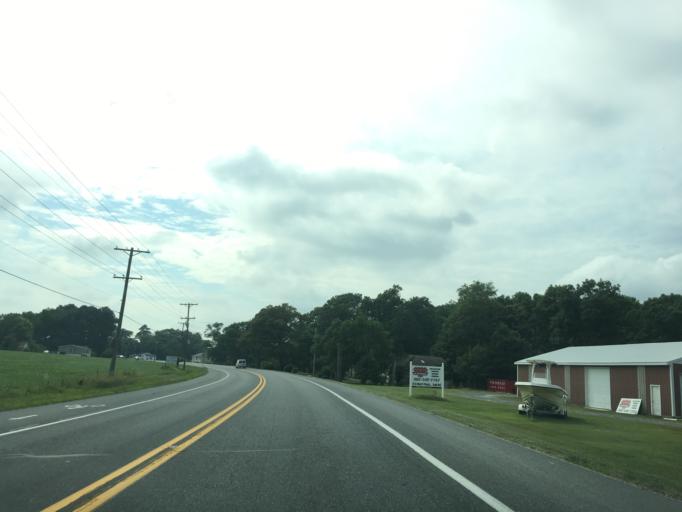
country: US
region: Delaware
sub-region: Sussex County
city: Long Neck
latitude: 38.5569
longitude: -75.1641
